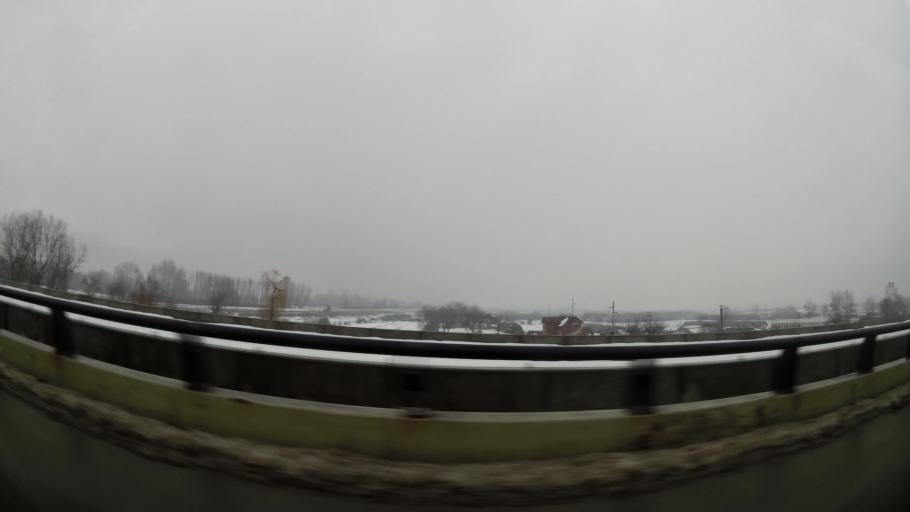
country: RS
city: Ostruznica
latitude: 44.7376
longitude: 20.3269
